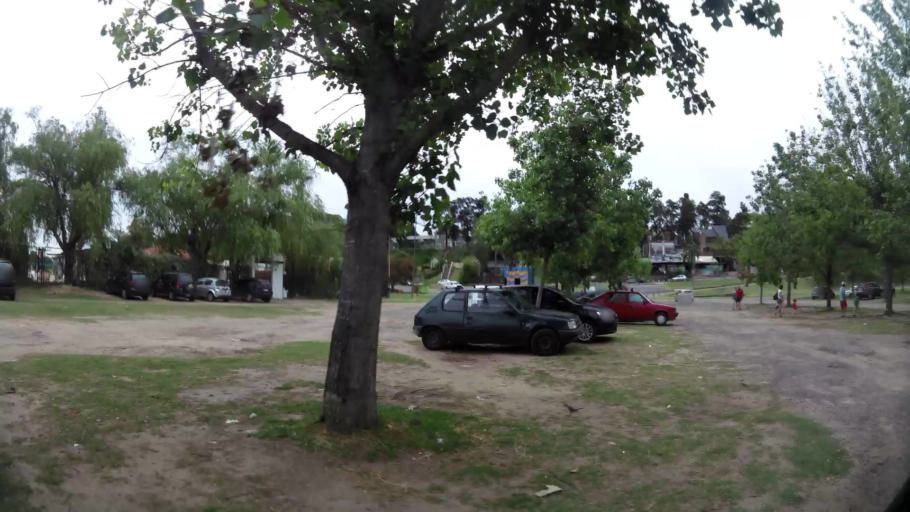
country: AR
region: Santa Fe
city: Granadero Baigorria
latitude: -32.8806
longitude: -60.6867
